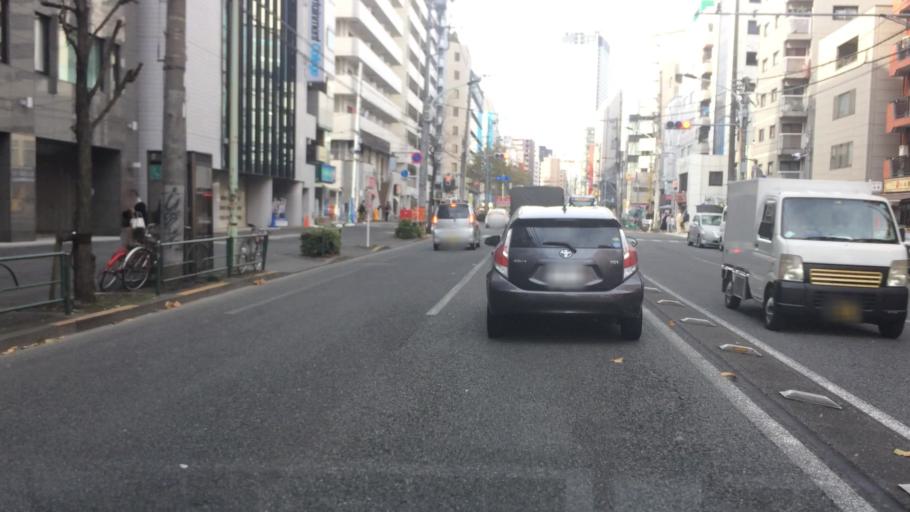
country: JP
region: Tokyo
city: Tokyo
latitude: 35.6470
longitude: 139.6952
